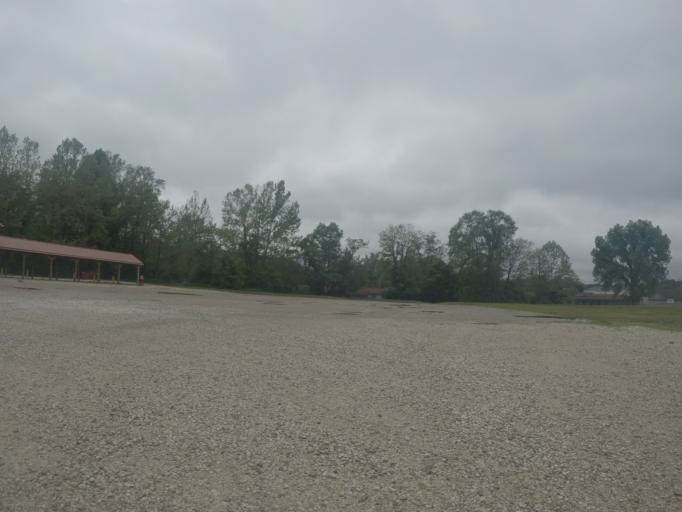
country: US
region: West Virginia
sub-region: Cabell County
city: Barboursville
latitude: 38.4111
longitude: -82.2981
